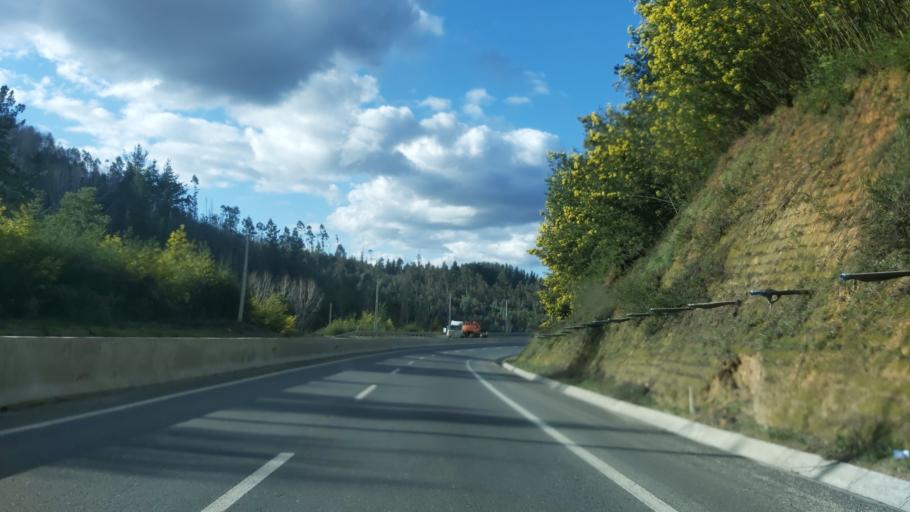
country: CL
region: Biobio
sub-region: Provincia de Concepcion
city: Penco
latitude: -36.8513
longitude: -72.9072
